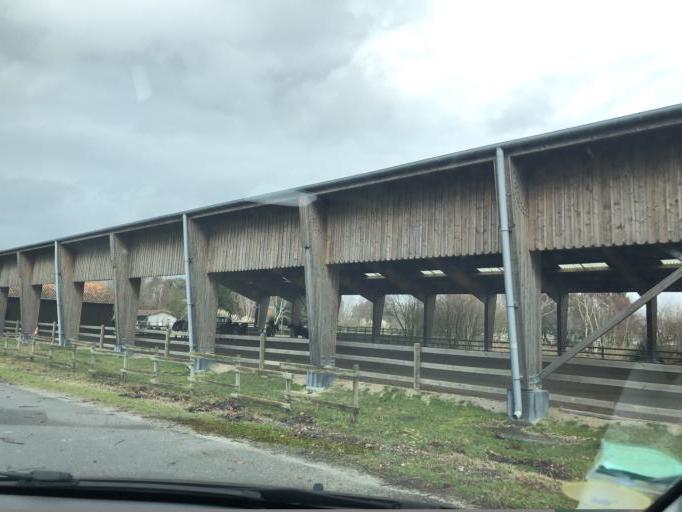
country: FR
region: Aquitaine
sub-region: Departement de la Gironde
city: Hourtin
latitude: 45.1779
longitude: -1.0747
